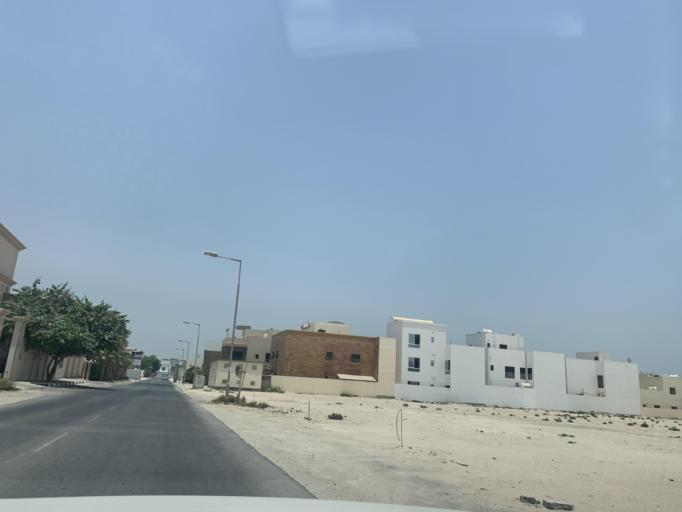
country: BH
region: Manama
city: Jidd Hafs
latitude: 26.2078
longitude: 50.4704
